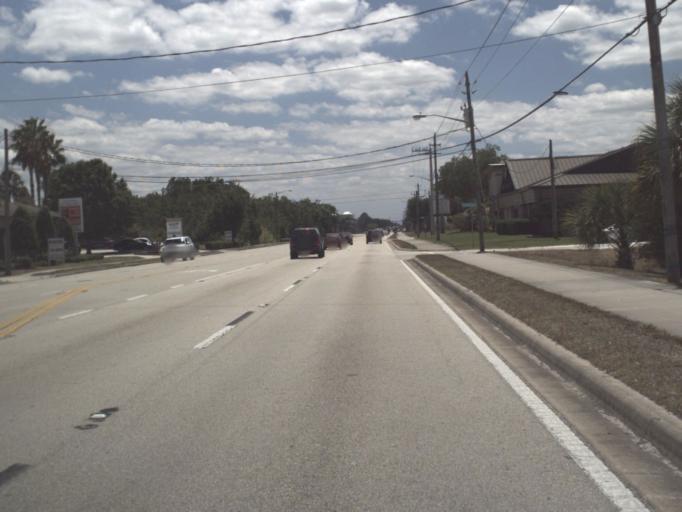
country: US
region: Florida
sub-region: Brevard County
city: Melbourne
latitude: 28.0729
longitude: -80.6214
